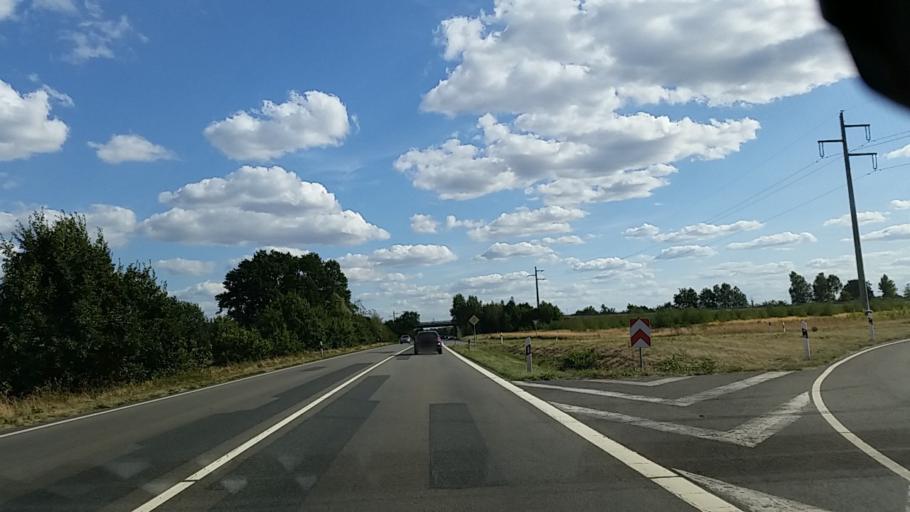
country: DE
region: Lower Saxony
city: Wagenhoff
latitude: 52.5105
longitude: 10.5227
